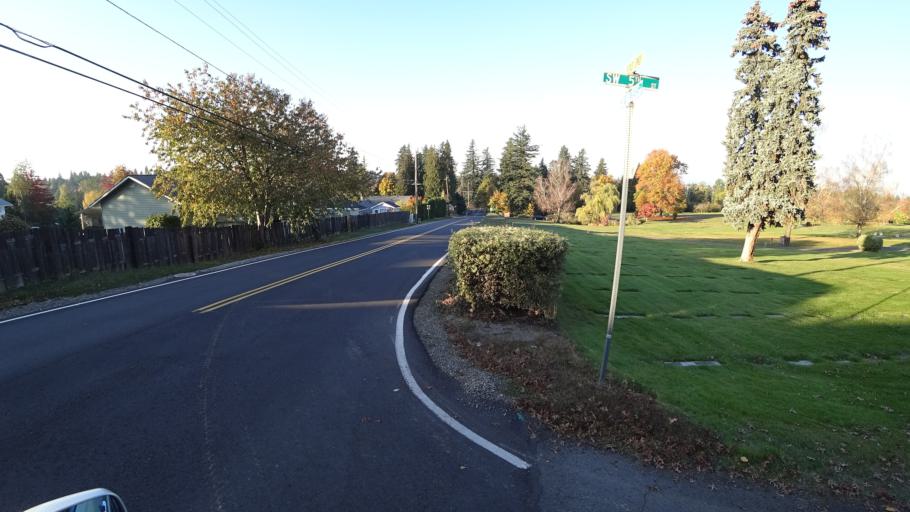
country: US
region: Oregon
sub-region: Multnomah County
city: Gresham
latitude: 45.4936
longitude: -122.4345
